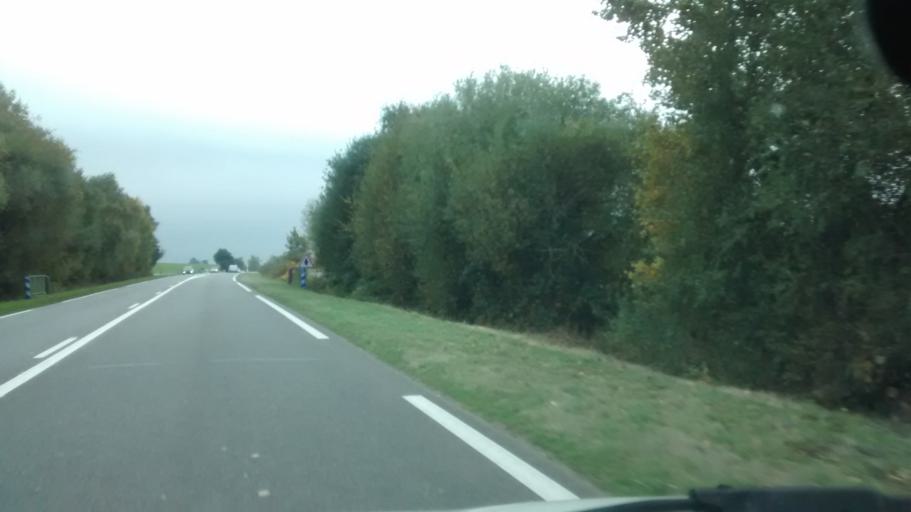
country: FR
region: Brittany
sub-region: Departement d'Ille-et-Vilaine
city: Acigne
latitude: 48.1405
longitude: -1.5163
